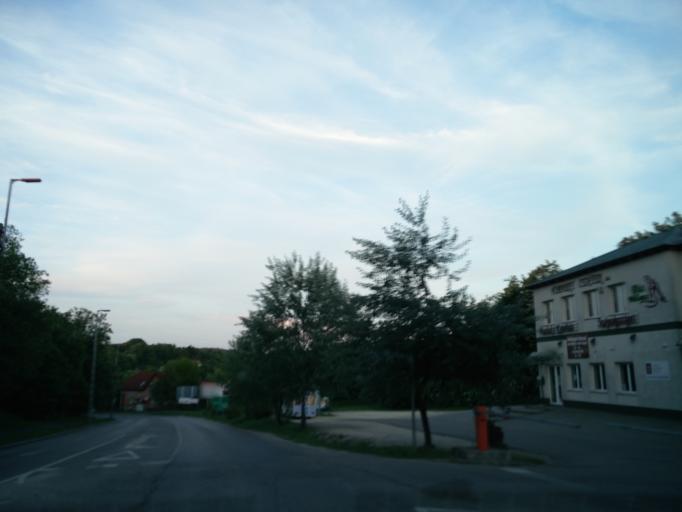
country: HU
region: Pest
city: Biatorbagy
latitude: 47.4711
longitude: 18.8305
